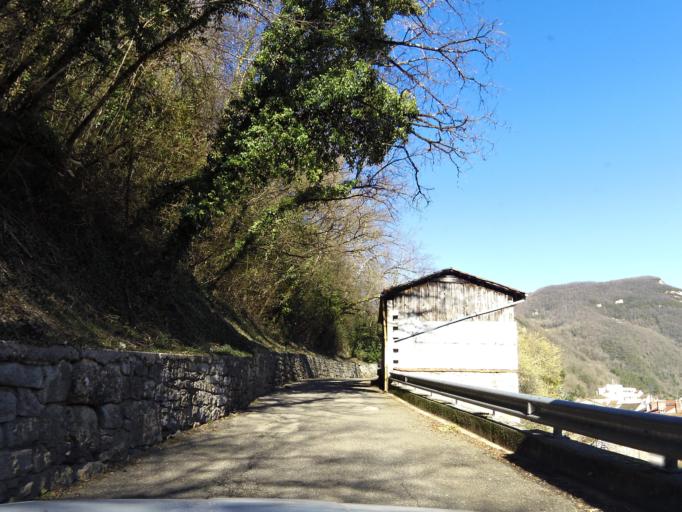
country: FR
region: Rhone-Alpes
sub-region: Departement de l'Ain
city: Saint-Rambert-en-Bugey
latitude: 45.9464
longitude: 5.4347
